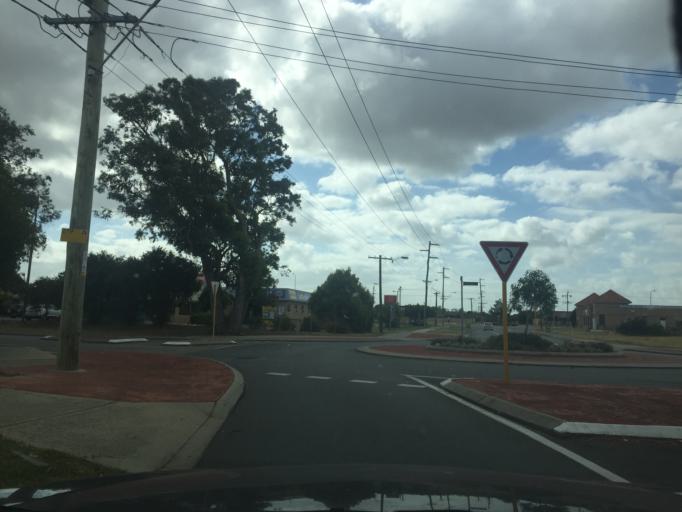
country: AU
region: Western Australia
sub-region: Gosnells
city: Maddington
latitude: -32.0511
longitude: 115.9778
